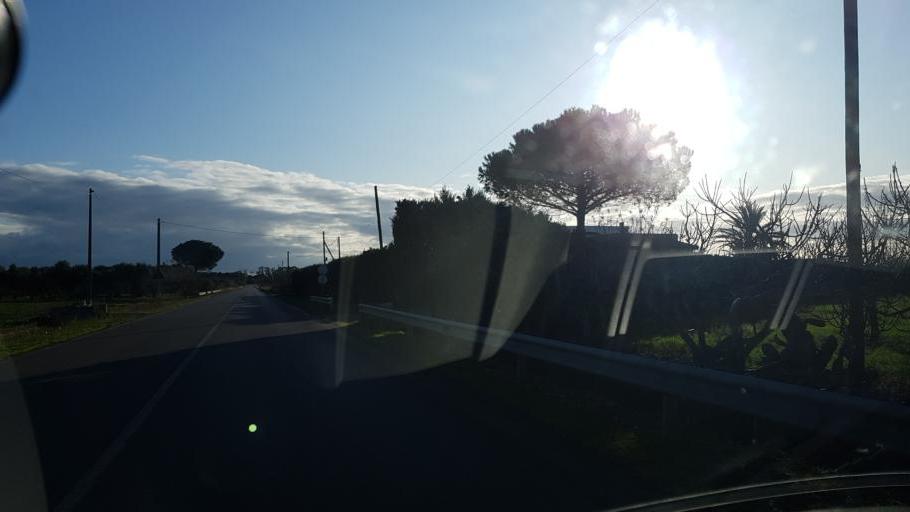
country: IT
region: Apulia
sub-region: Provincia di Brindisi
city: Tuturano
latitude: 40.5603
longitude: 18.0133
